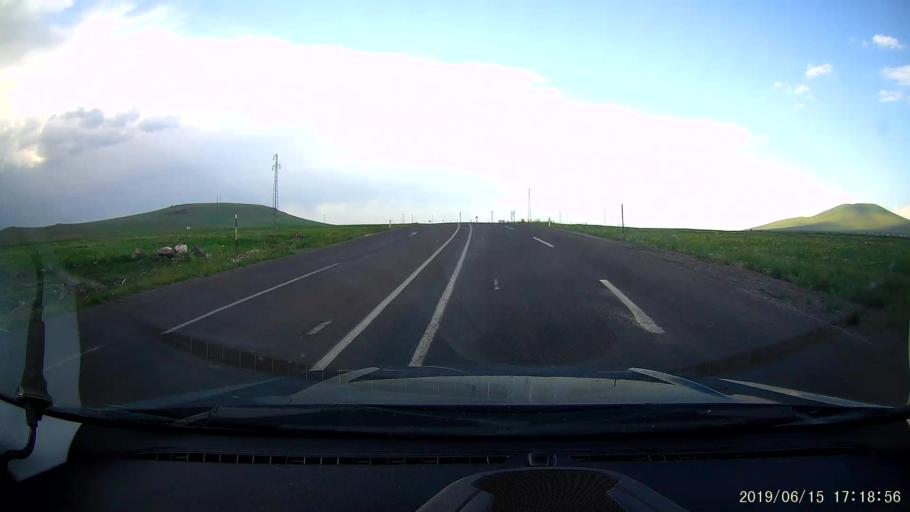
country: TR
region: Kars
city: Kars
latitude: 40.6143
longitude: 43.2685
